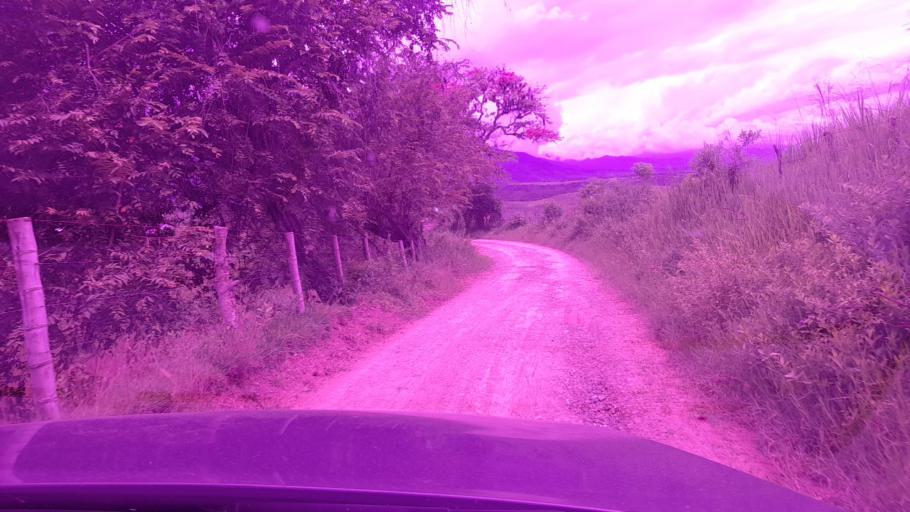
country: CO
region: Valle del Cauca
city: Andalucia
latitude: 4.1691
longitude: -76.0926
